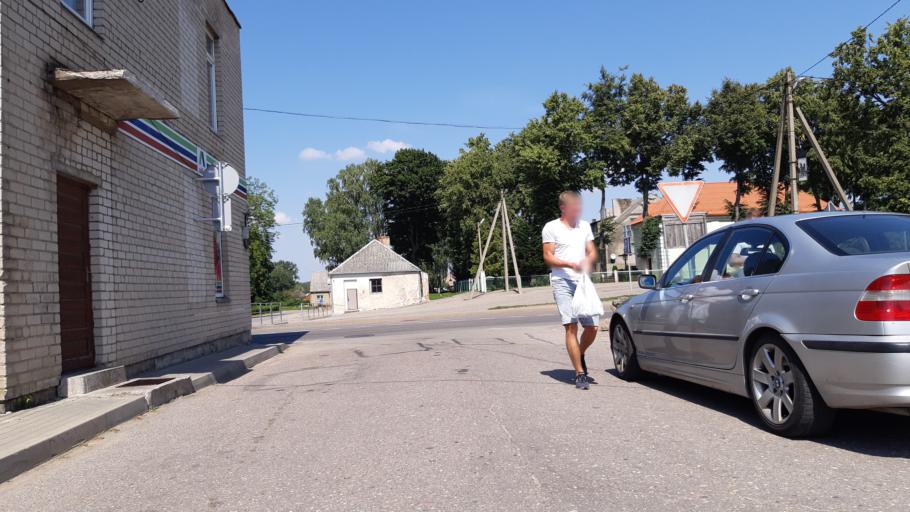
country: LT
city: Virbalis
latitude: 54.6254
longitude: 22.8218
